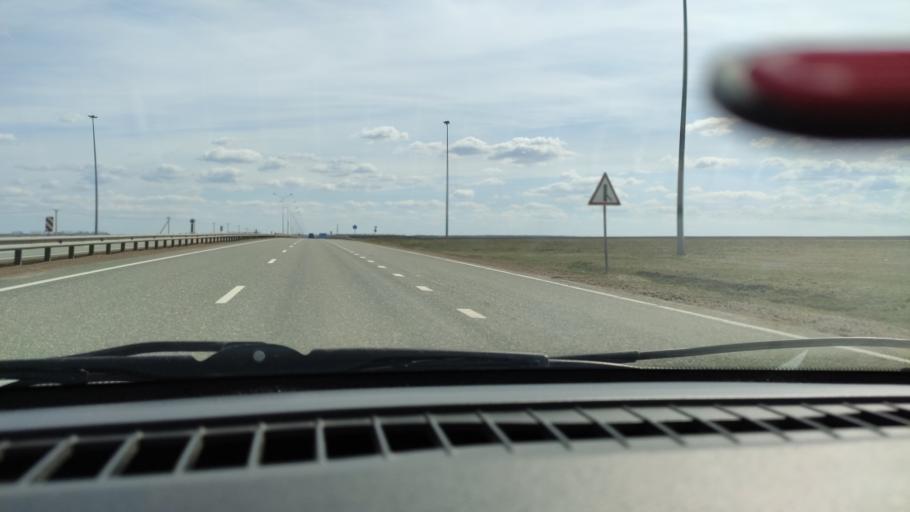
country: RU
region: Bashkortostan
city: Kushnarenkovo
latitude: 55.0741
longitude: 55.2846
